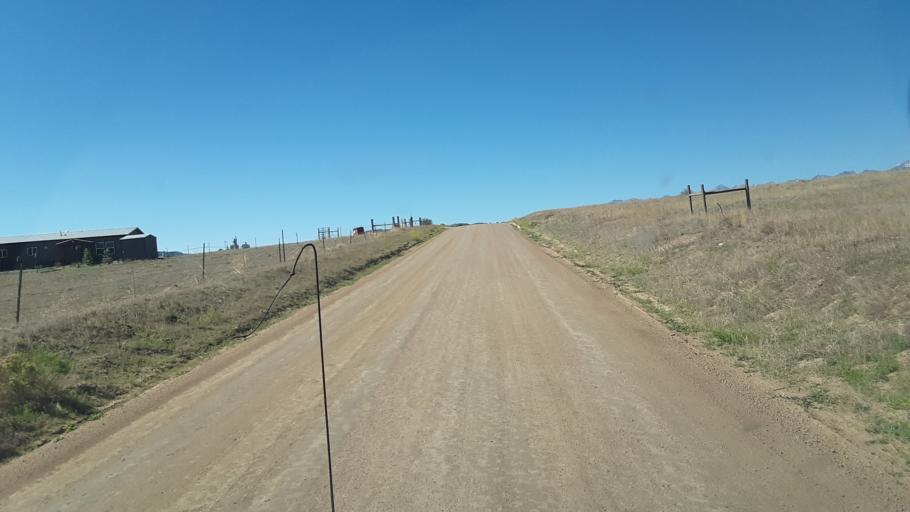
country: US
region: Colorado
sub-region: Custer County
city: Westcliffe
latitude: 38.2886
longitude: -105.4911
